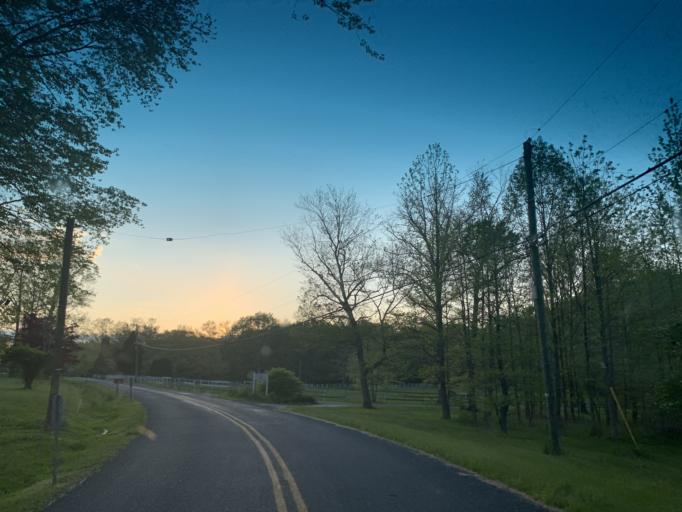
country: US
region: Maryland
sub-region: Harford County
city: Riverside
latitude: 39.5247
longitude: -76.2424
